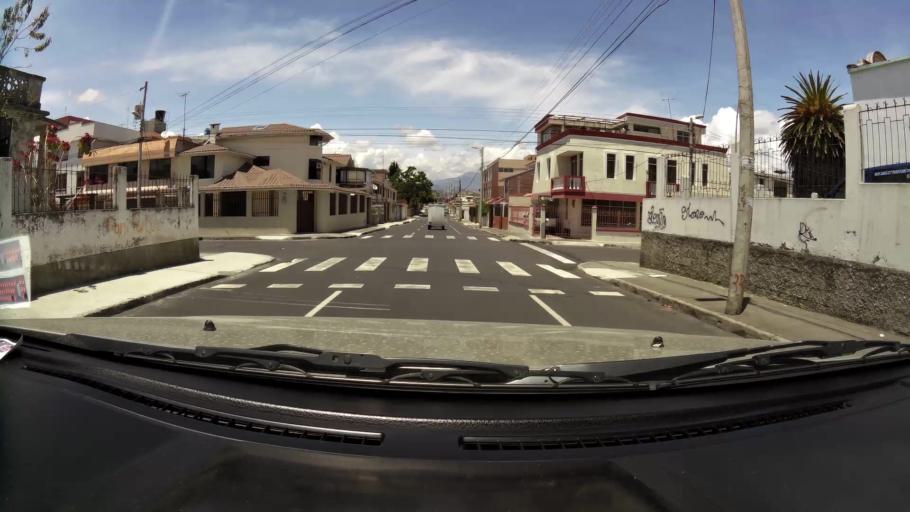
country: EC
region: Chimborazo
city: Riobamba
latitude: -1.6748
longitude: -78.6398
